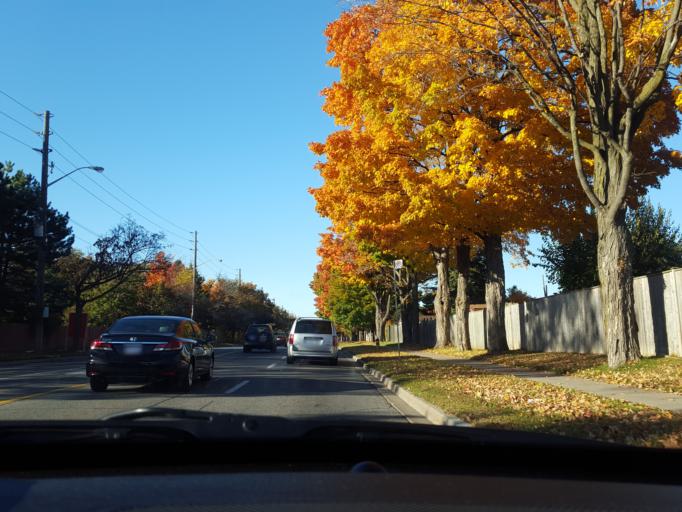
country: CA
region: Ontario
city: Scarborough
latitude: 43.7986
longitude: -79.2734
